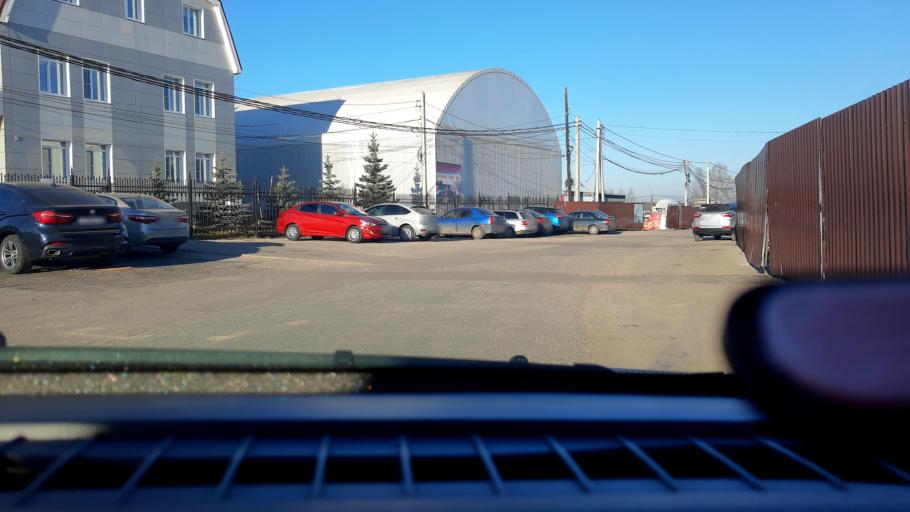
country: RU
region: Nizjnij Novgorod
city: Gorbatovka
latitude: 56.3834
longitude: 43.7989
